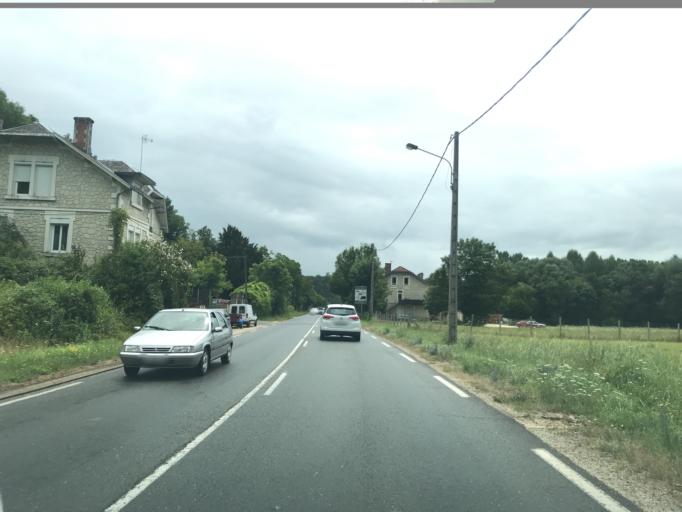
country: FR
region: Aquitaine
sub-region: Departement de la Dordogne
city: Chancelade
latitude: 45.2409
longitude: 0.6852
